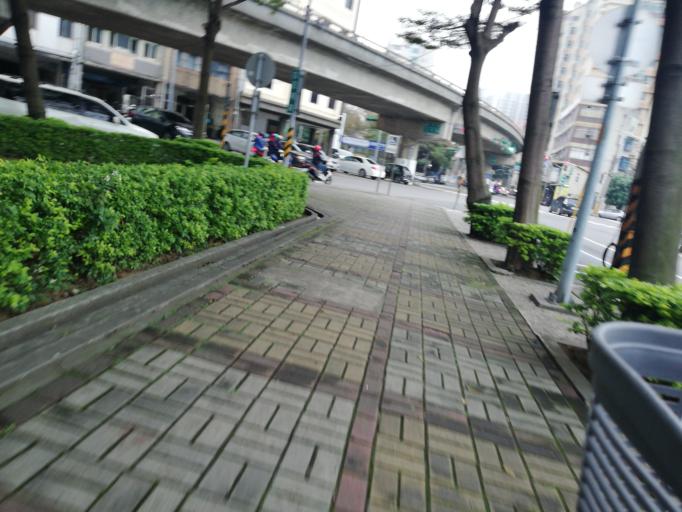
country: TW
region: Taiwan
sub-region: Taoyuan
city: Taoyuan
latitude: 24.9864
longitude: 121.3113
